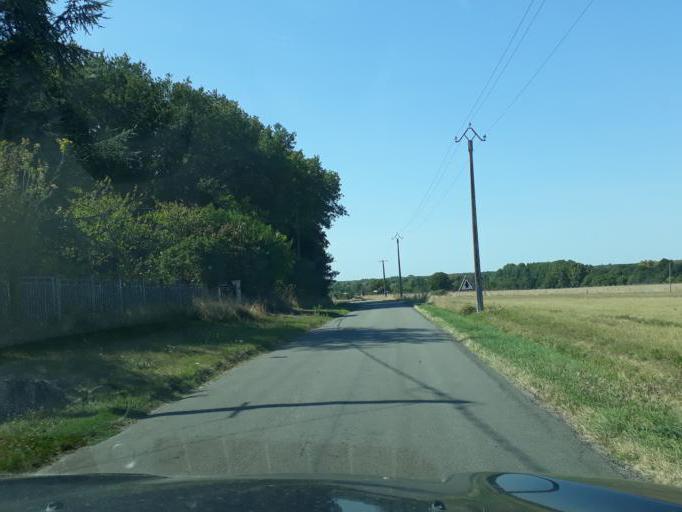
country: FR
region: Centre
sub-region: Departement du Loir-et-Cher
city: Gievres
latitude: 47.2588
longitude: 1.6933
